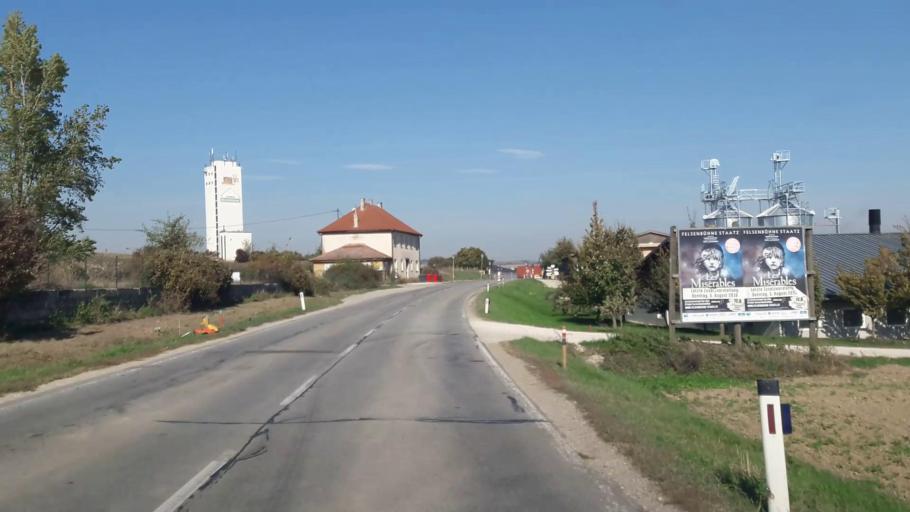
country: AT
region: Lower Austria
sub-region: Politischer Bezirk Korneuburg
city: Grossrussbach
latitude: 48.4730
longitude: 16.3801
